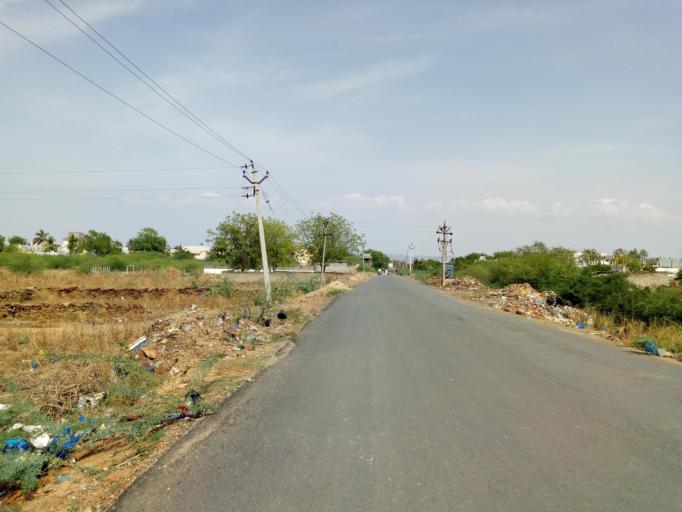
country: IN
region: Andhra Pradesh
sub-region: Prakasam
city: Cumbum
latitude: 15.5853
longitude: 79.1083
